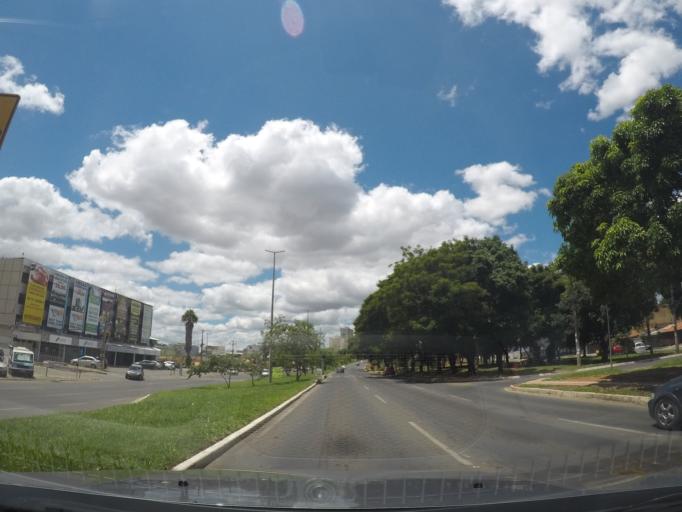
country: BR
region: Federal District
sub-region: Brasilia
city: Brasilia
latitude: -15.8386
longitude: -47.9849
